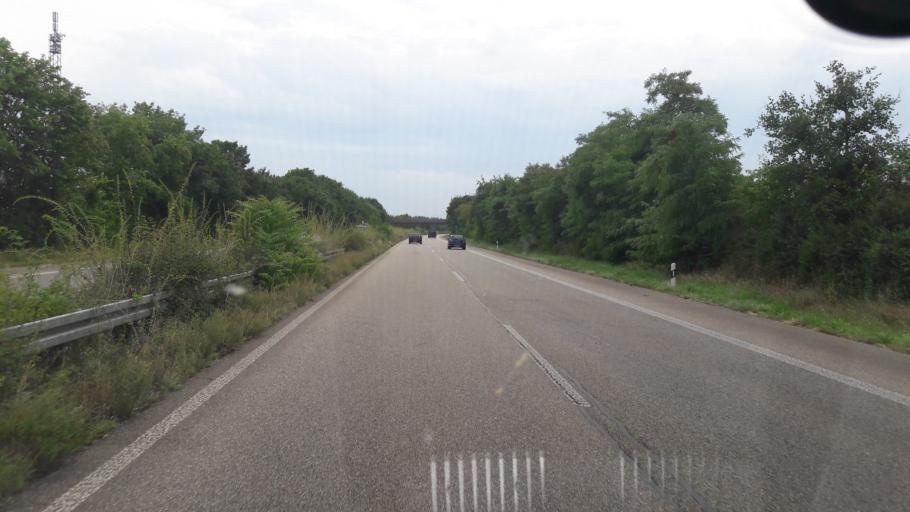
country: DE
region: Baden-Wuerttemberg
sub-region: Karlsruhe Region
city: Eggenstein-Leopoldshafen
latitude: 49.0772
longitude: 8.4077
